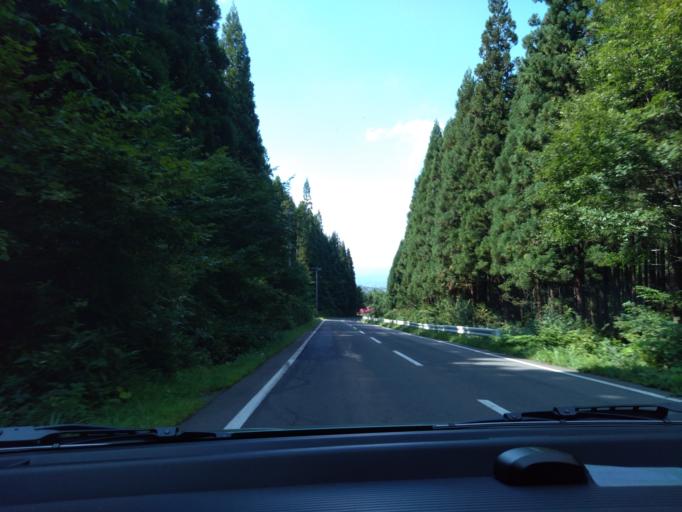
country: JP
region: Iwate
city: Shizukuishi
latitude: 39.6392
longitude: 141.0062
